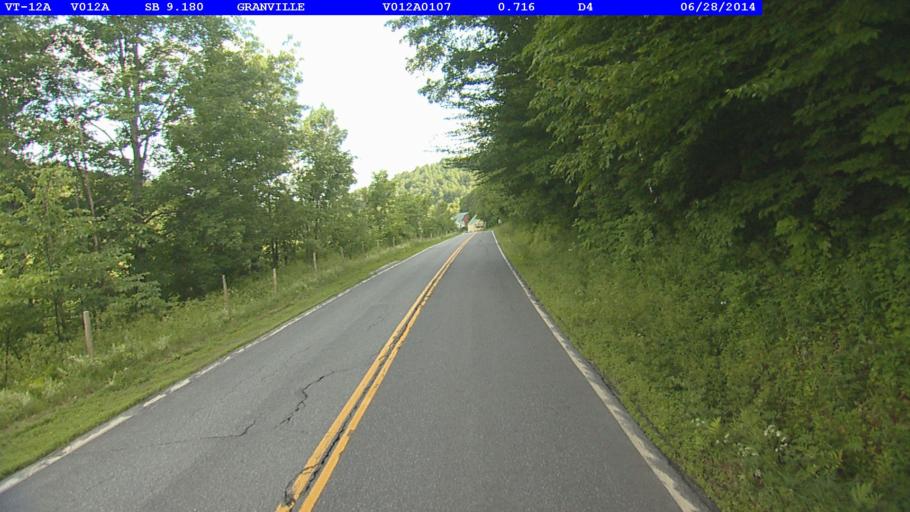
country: US
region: Vermont
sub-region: Orange County
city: Randolph
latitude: 44.0204
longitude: -72.7601
